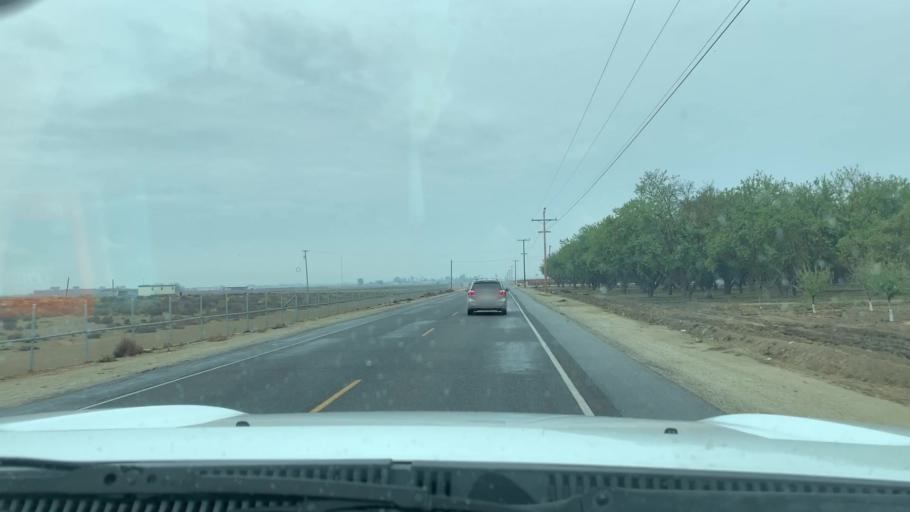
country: US
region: California
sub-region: Kern County
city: Delano
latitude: 35.7613
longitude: -119.3141
